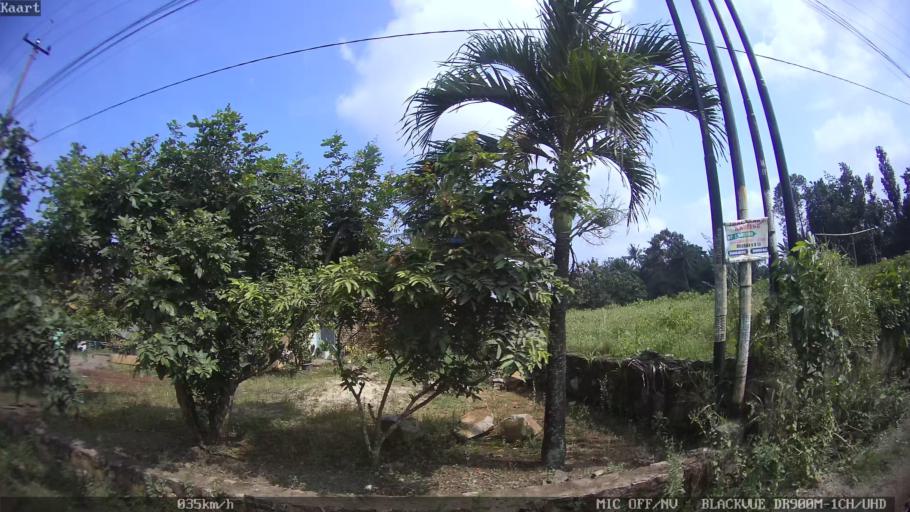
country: ID
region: Lampung
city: Kedaton
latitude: -5.3399
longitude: 105.2737
